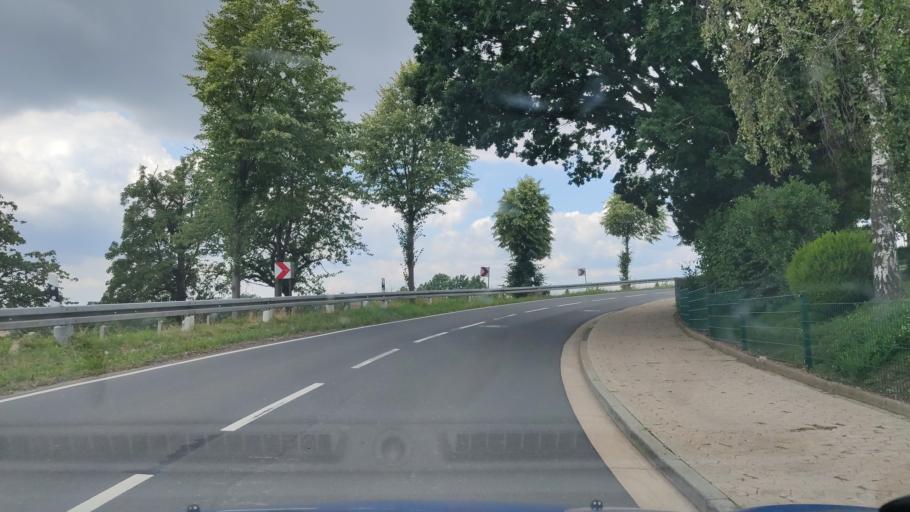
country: DE
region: Lower Saxony
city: Coppenbrugge
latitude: 52.1056
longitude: 9.5006
